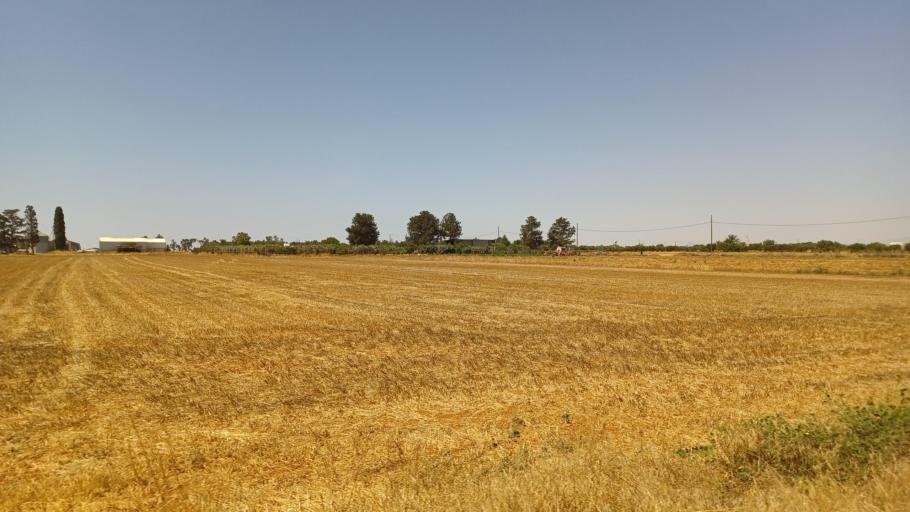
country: CY
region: Larnaka
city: Xylotymbou
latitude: 35.0284
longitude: 33.7322
